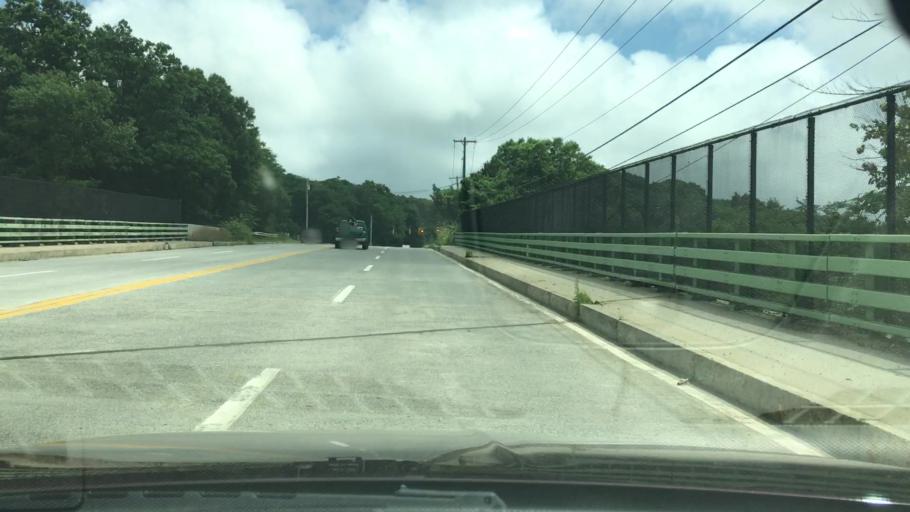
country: US
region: New York
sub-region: Suffolk County
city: Commack
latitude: 40.8159
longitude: -73.2892
